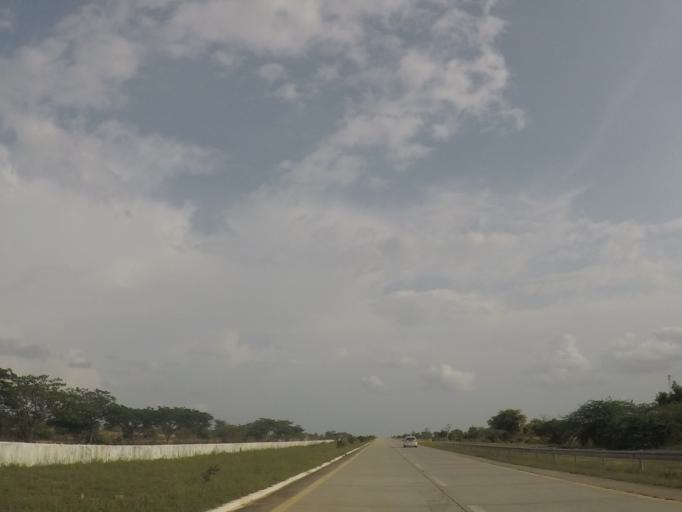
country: MM
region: Mandalay
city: Meiktila
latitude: 20.5415
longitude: 95.8142
